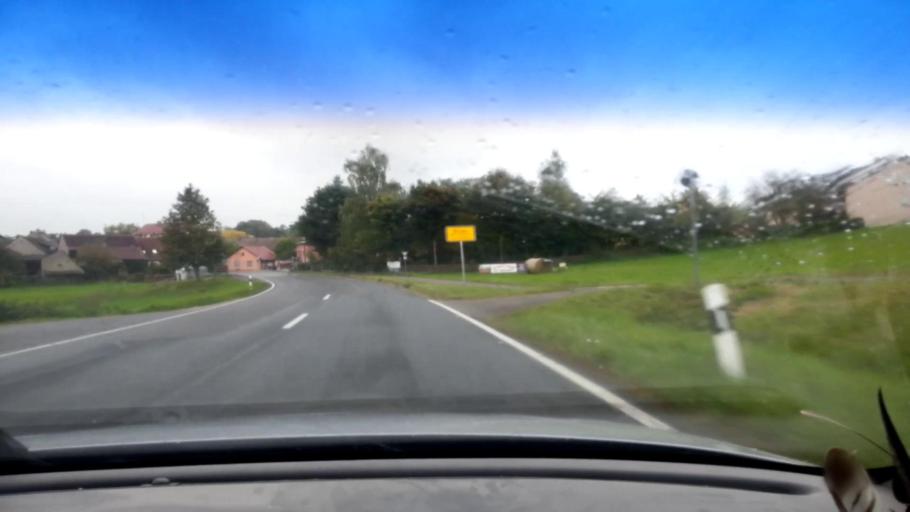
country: DE
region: Bavaria
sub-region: Upper Franconia
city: Walsdorf
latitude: 49.8723
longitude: 10.8028
